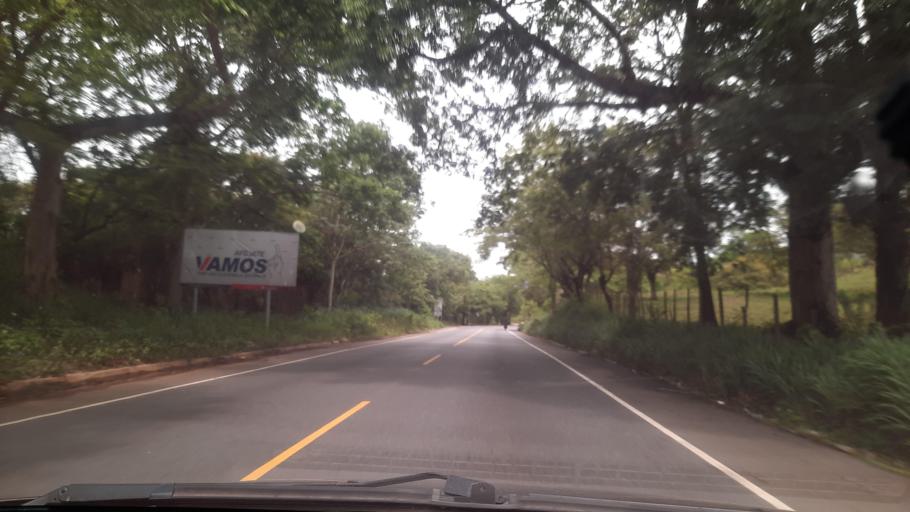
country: GT
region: Izabal
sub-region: Municipio de Los Amates
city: Los Amates
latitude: 15.2327
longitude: -89.1906
